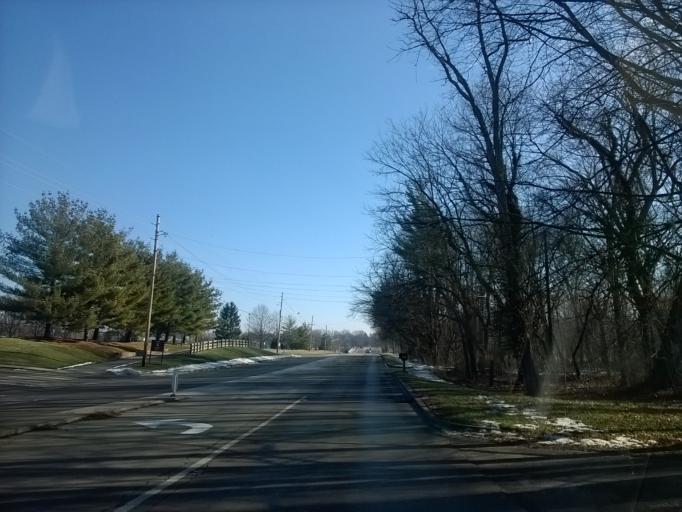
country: US
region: Indiana
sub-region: Hamilton County
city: Carmel
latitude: 39.9857
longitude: -86.1222
